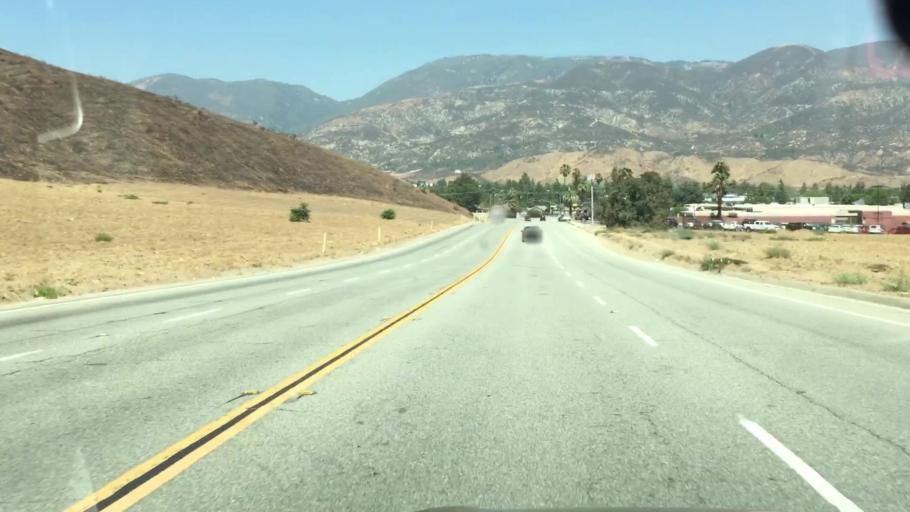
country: US
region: California
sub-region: San Bernardino County
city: Muscoy
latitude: 34.1640
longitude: -117.3176
